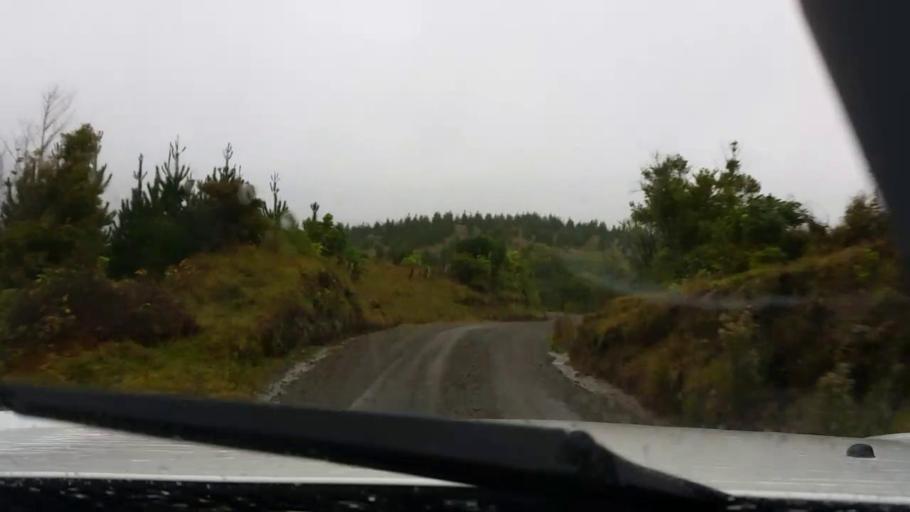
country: NZ
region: Wellington
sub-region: Masterton District
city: Masterton
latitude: -41.2049
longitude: 175.8134
